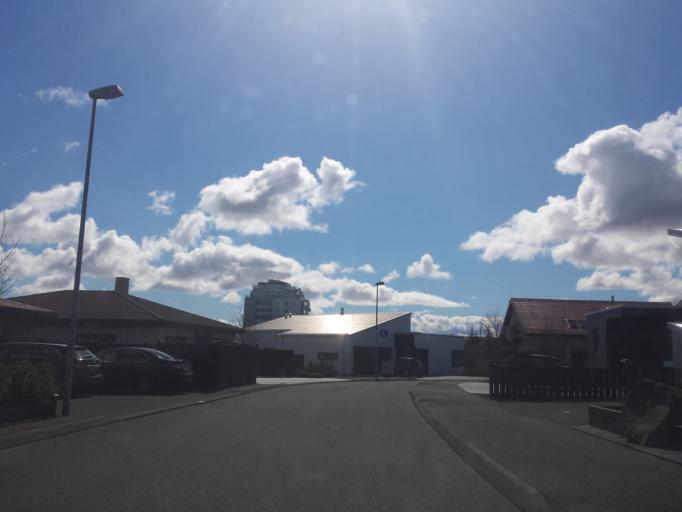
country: IS
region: Capital Region
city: Reykjavik
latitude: 64.0919
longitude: -21.8442
